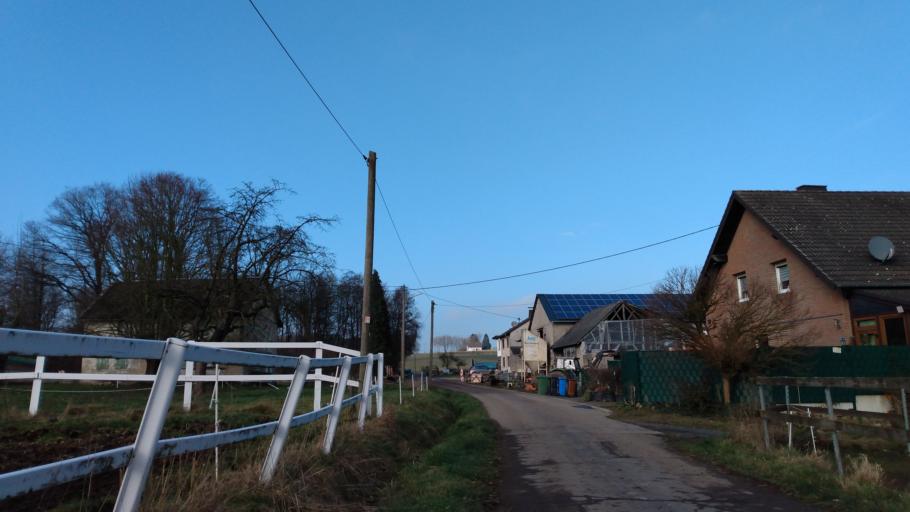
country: DE
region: Rheinland-Pfalz
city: Hirz-Maulsbach
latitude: 50.6815
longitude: 7.4604
